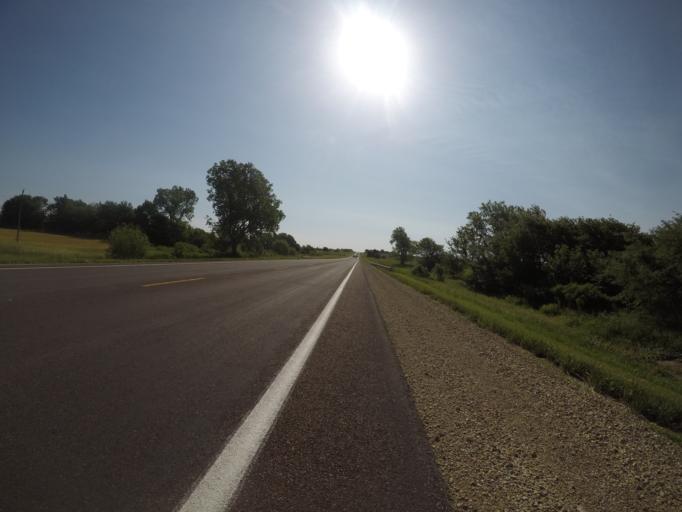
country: US
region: Kansas
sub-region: Riley County
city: Fort Riley North
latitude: 39.3064
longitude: -96.8907
